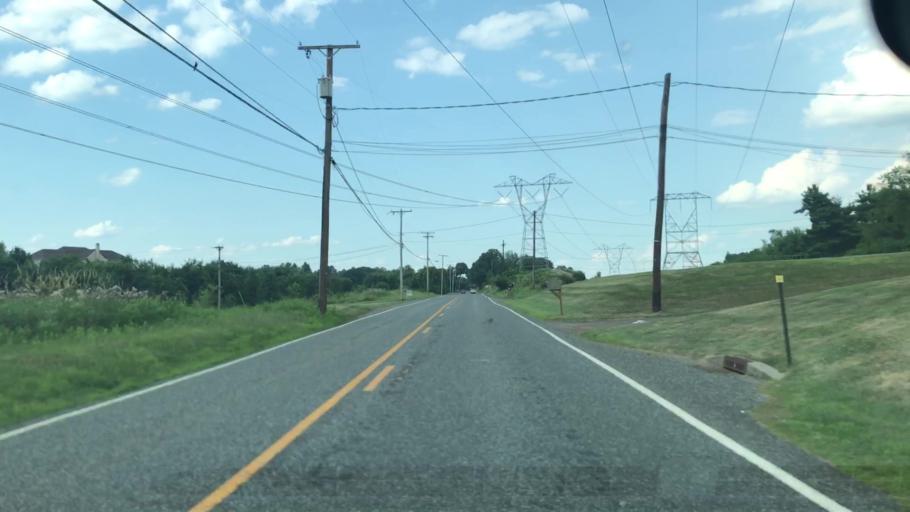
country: US
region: New Jersey
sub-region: Hunterdon County
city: Flemington
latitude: 40.4929
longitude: -74.8111
